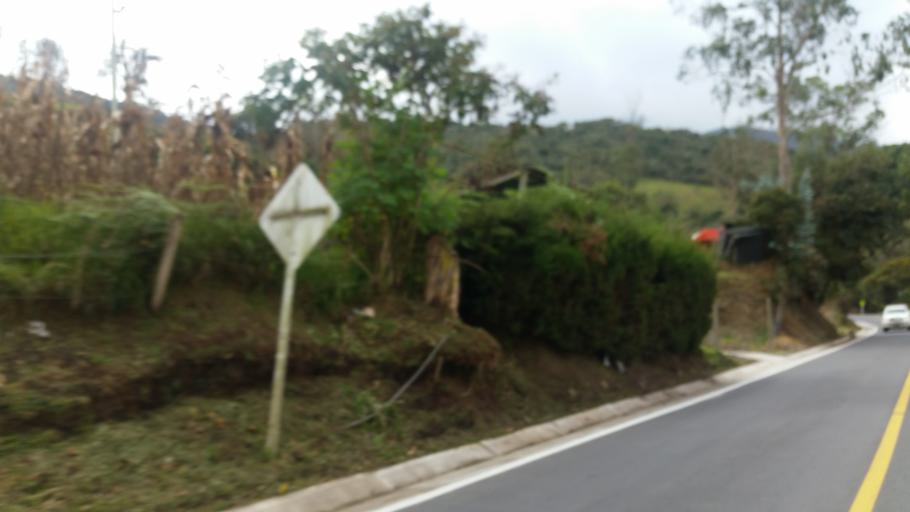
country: CO
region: Cundinamarca
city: Choachi
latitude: 4.5545
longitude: -73.9452
